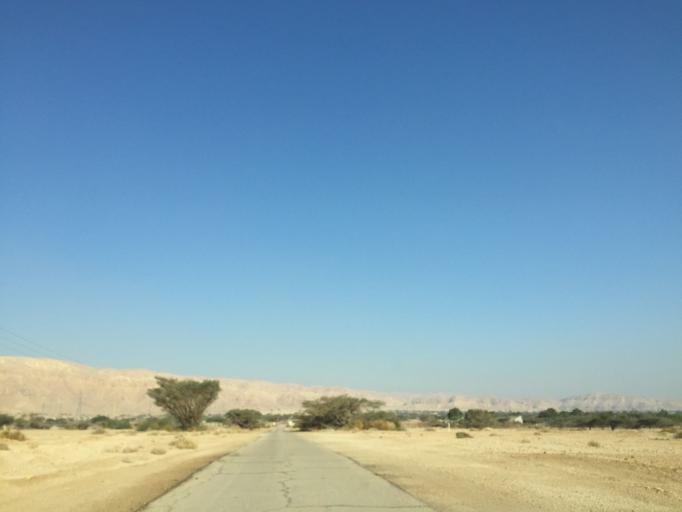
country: JO
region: Ma'an
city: Al Quwayrah
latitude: 29.8430
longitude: 35.0295
